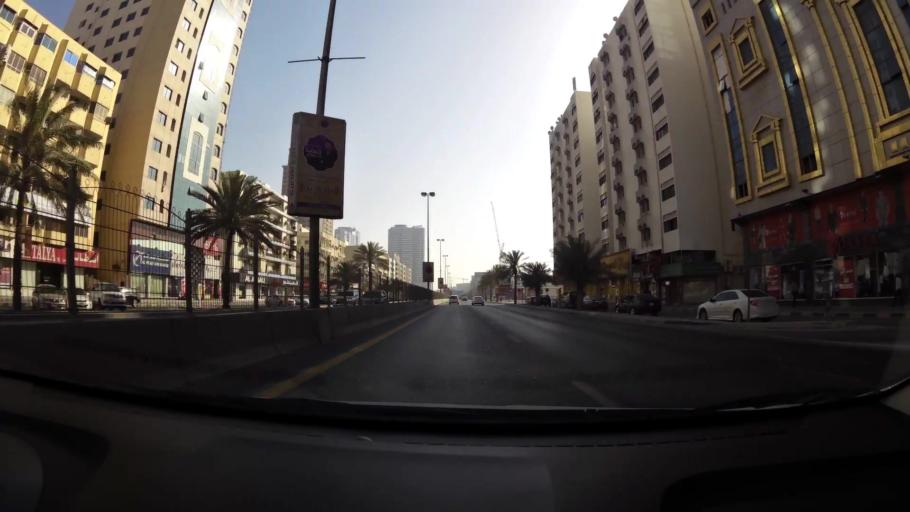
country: AE
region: Ash Shariqah
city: Sharjah
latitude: 25.3231
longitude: 55.3903
